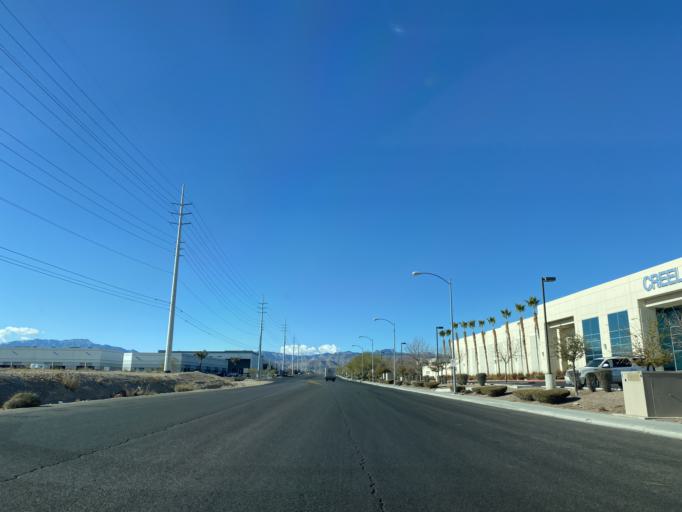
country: US
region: Nevada
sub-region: Clark County
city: Spring Valley
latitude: 36.0709
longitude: -115.2291
